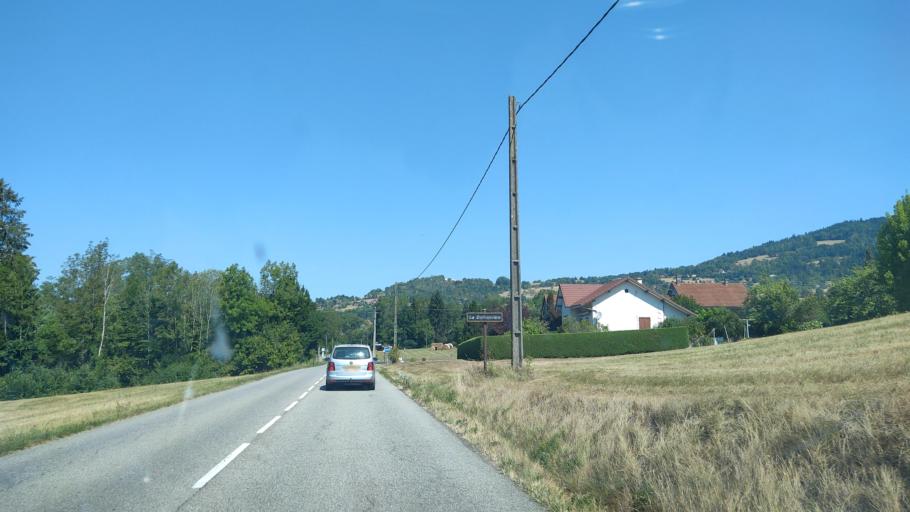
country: FR
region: Rhone-Alpes
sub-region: Departement de la Savoie
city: Novalaise
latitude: 45.5900
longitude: 5.7823
